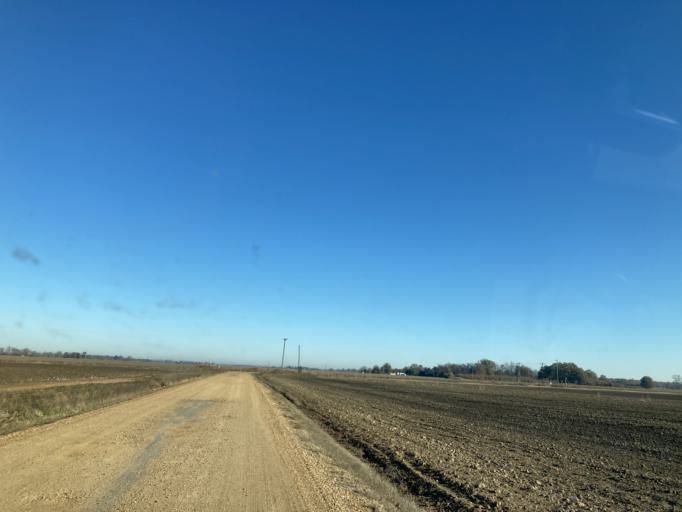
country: US
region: Mississippi
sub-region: Yazoo County
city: Yazoo City
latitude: 32.9210
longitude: -90.5941
